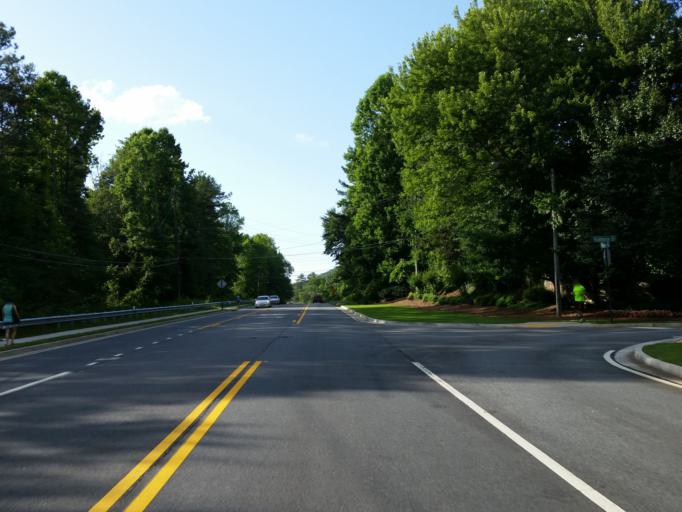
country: US
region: Georgia
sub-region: Cherokee County
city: Woodstock
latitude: 34.0522
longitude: -84.4556
